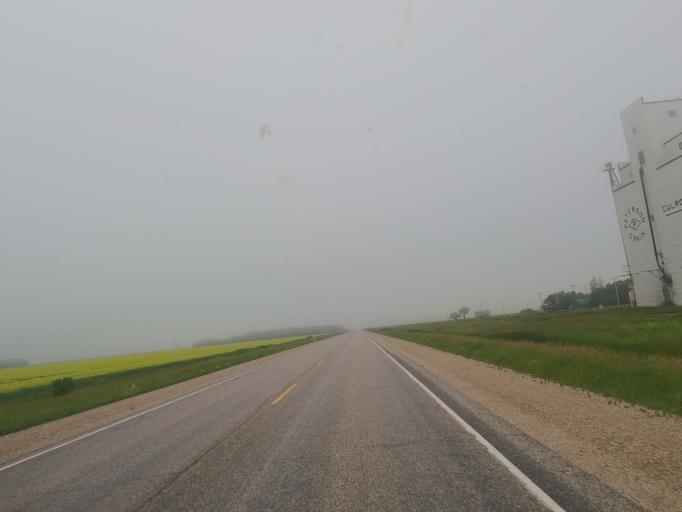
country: CA
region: Manitoba
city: Carman
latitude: 49.7147
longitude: -97.9073
